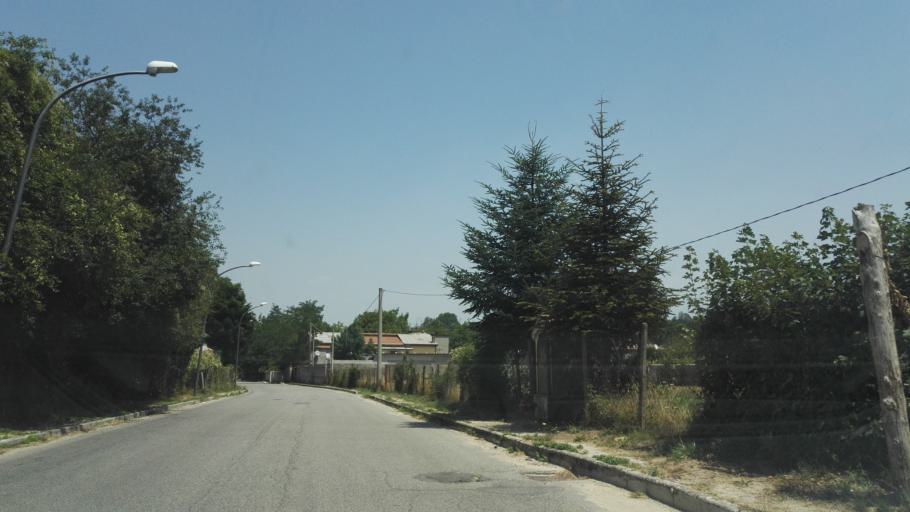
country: IT
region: Calabria
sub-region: Provincia di Vibo-Valentia
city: Serra San Bruno
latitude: 38.5742
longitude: 16.3312
